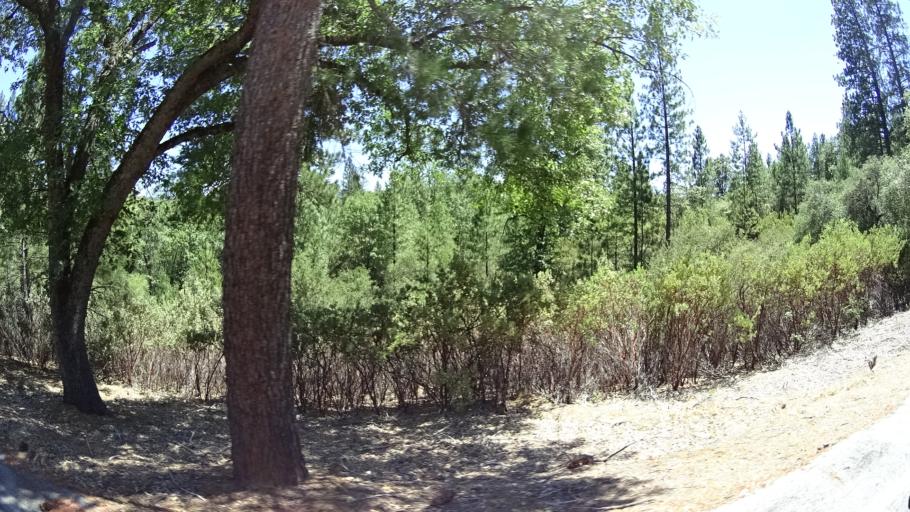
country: US
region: California
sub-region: Calaveras County
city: Forest Meadows
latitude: 38.2151
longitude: -120.4448
